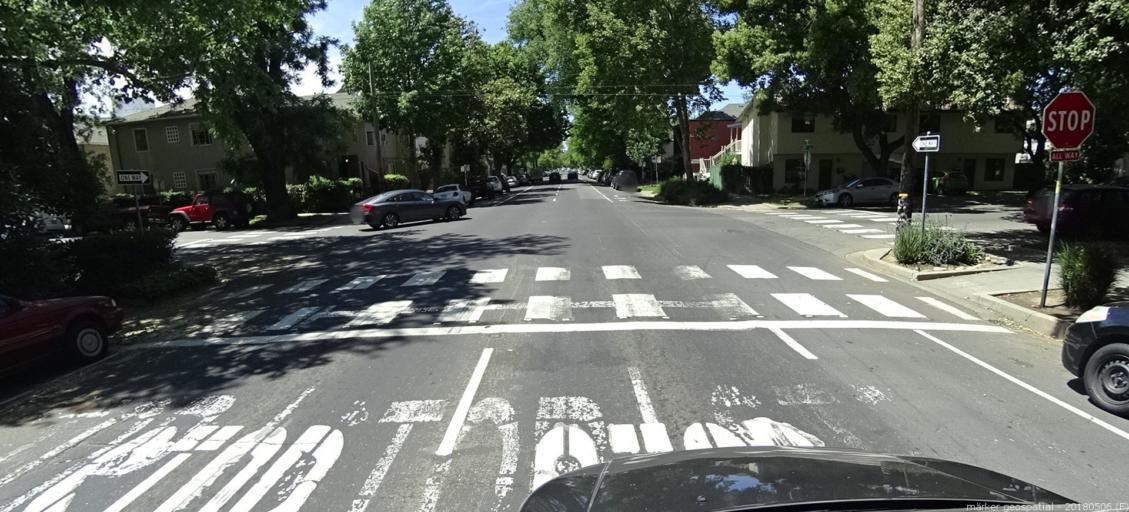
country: US
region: California
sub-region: Sacramento County
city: Sacramento
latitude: 38.5686
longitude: -121.4772
